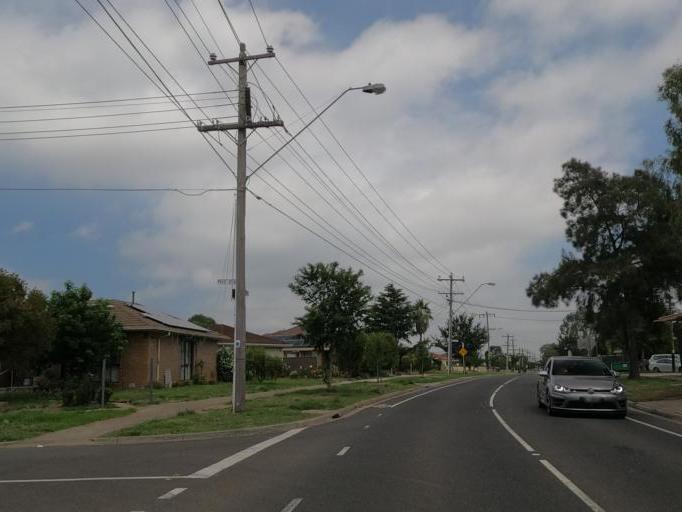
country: AU
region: Victoria
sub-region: Hume
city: Gladstone Park
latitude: -37.6897
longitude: 144.8983
